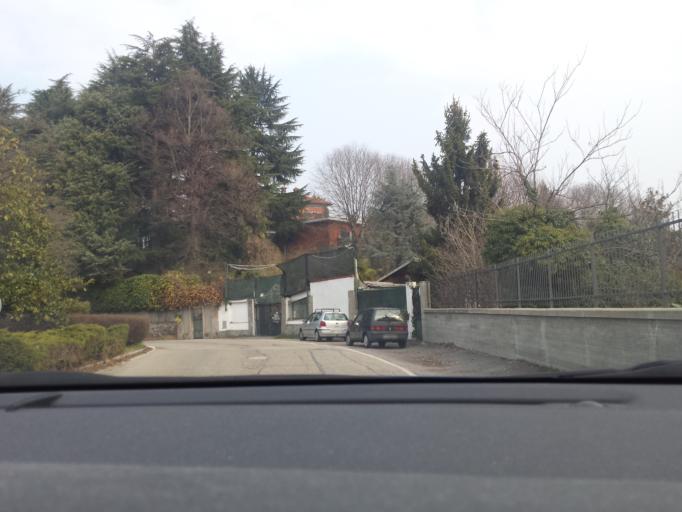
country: IT
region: Piedmont
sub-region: Provincia di Torino
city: Turin
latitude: 45.0543
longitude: 7.7161
